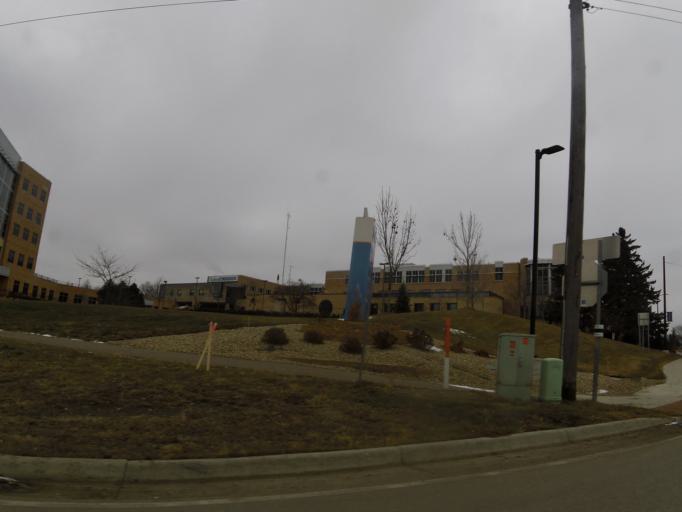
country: US
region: Minnesota
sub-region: Carver County
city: Waconia
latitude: 44.8420
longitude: -93.7909
